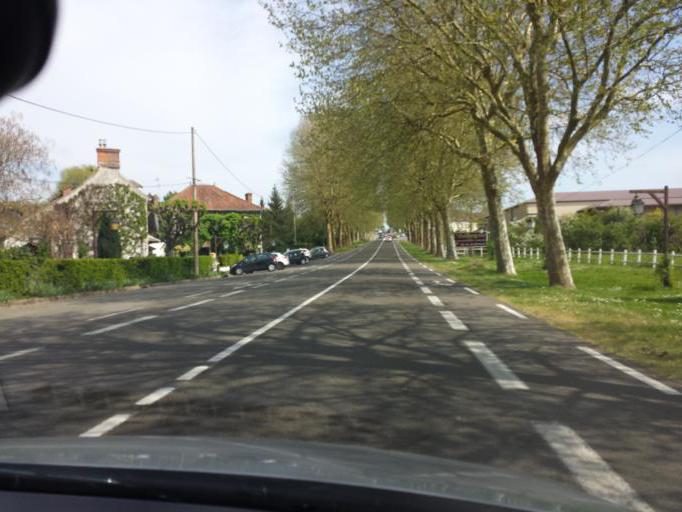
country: FR
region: Ile-de-France
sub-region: Departement des Yvelines
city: Villiers-Saint-Frederic
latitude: 48.8067
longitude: 1.8897
